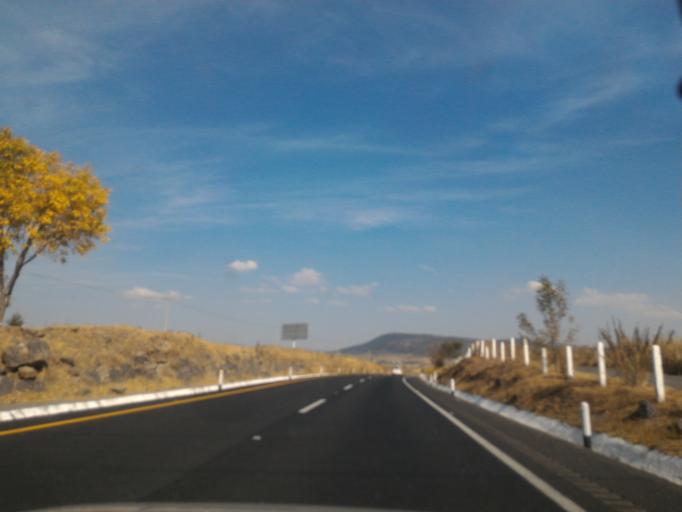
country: MX
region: Michoacan
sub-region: Contepec
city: El Cesped
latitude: 19.8790
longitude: -100.1683
